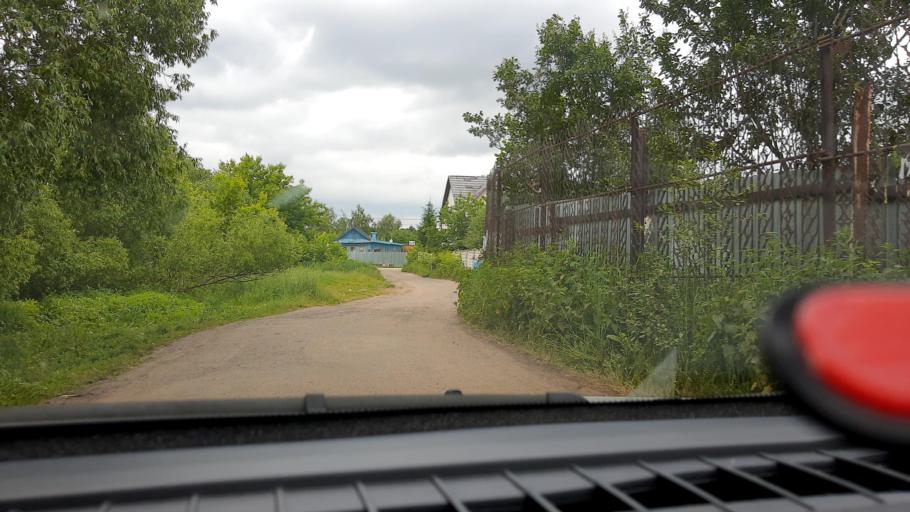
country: RU
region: Nizjnij Novgorod
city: Burevestnik
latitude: 56.2140
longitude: 43.8382
